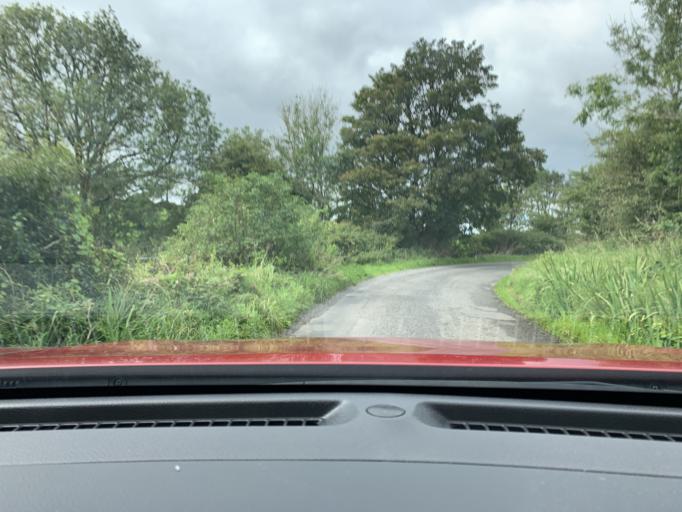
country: IE
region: Connaught
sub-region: Sligo
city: Collooney
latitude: 54.1592
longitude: -8.4303
